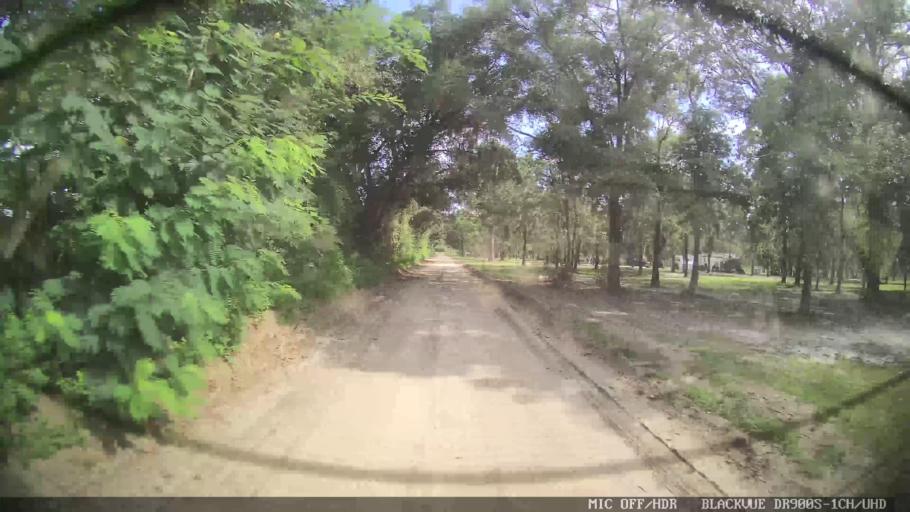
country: US
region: Georgia
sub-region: Echols County
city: Statenville
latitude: 30.6245
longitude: -83.1869
